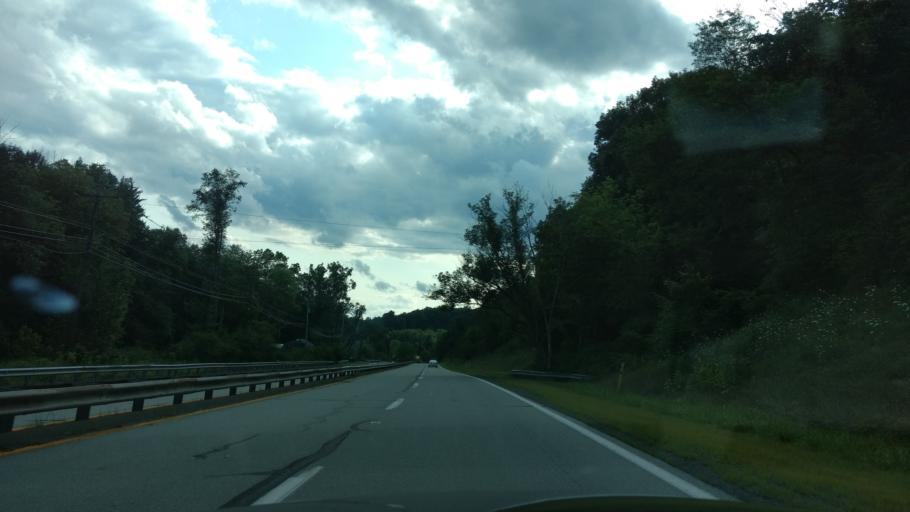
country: US
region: Pennsylvania
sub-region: Allegheny County
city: Plum
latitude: 40.5079
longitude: -79.6719
